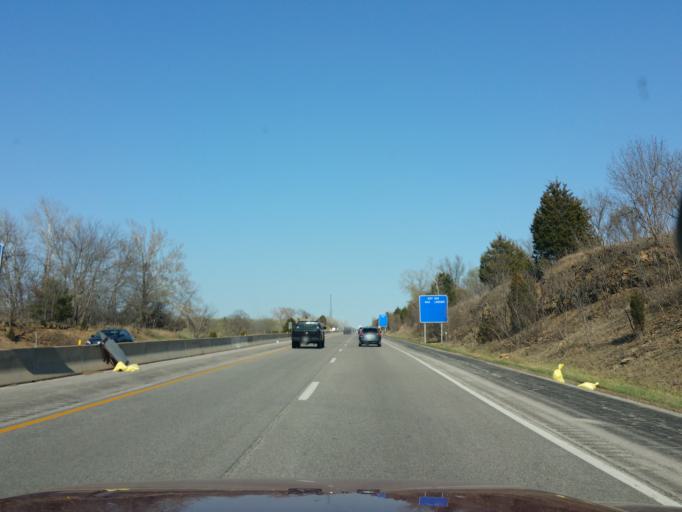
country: US
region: Kansas
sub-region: Wyandotte County
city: Bonner Springs
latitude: 39.0905
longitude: -94.9080
